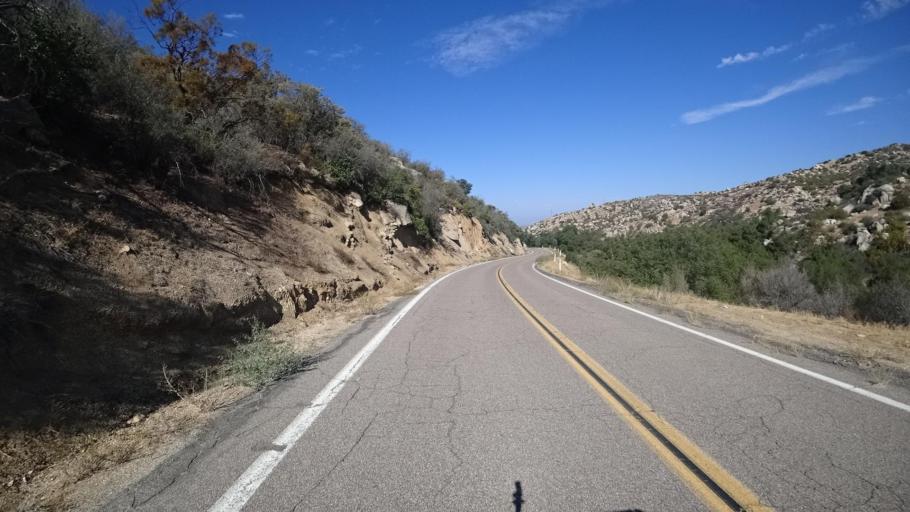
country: US
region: California
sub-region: Riverside County
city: Aguanga
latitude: 33.3733
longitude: -116.7141
